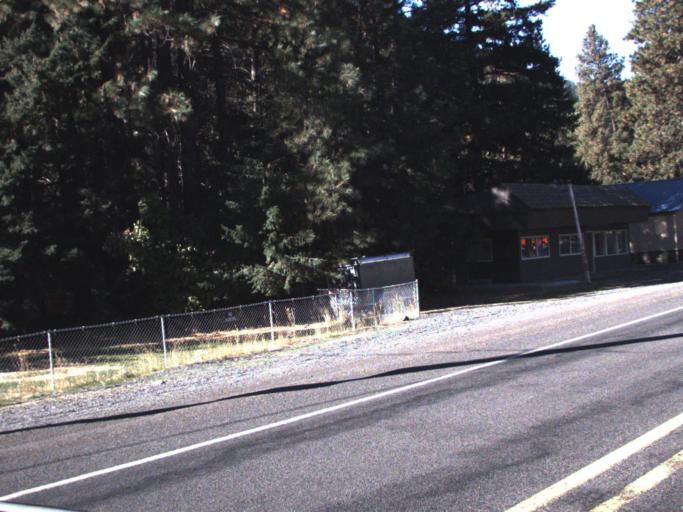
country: US
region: Washington
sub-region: Yakima County
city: Tieton
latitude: 46.6708
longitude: -120.9910
